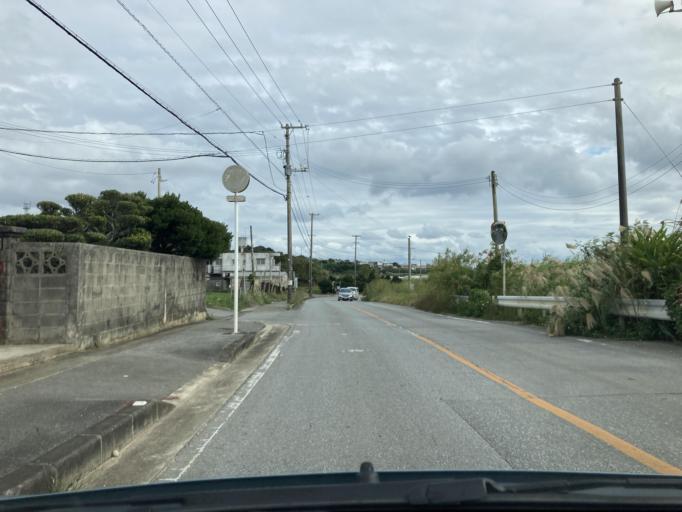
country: JP
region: Okinawa
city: Itoman
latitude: 26.1163
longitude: 127.6963
